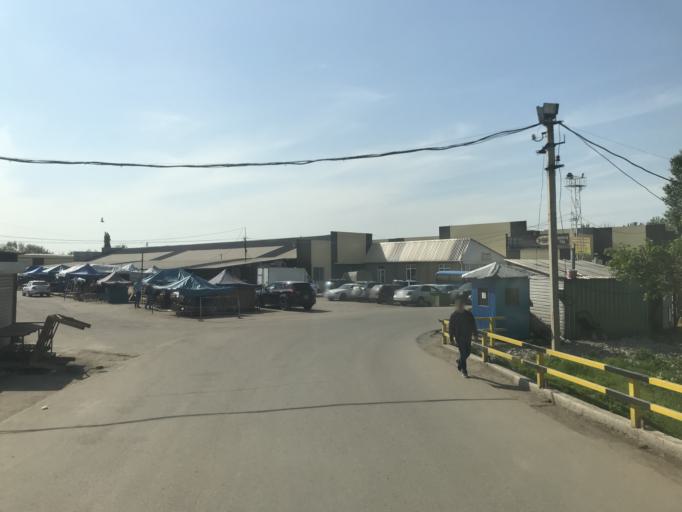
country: KZ
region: Almaty Oblysy
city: Burunday
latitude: 43.2324
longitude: 76.7701
